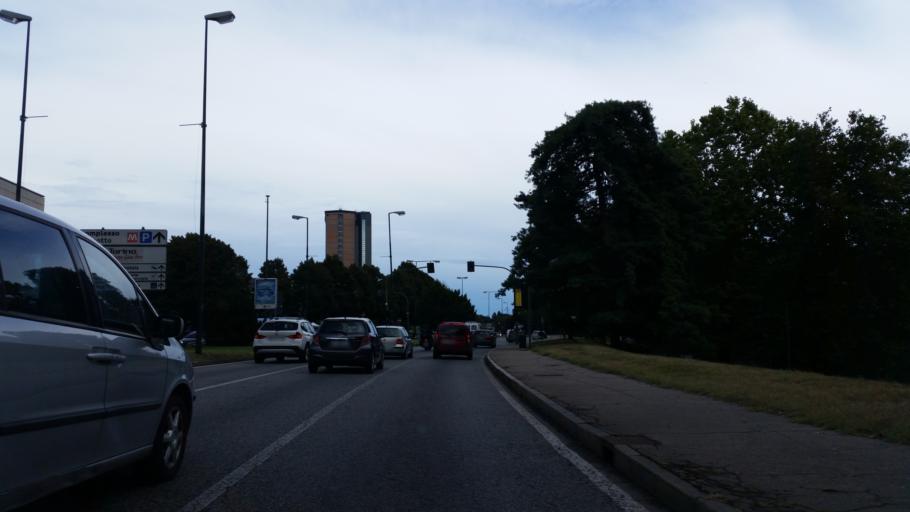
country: IT
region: Piedmont
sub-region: Provincia di Torino
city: Moncalieri
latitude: 45.0292
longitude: 7.6728
